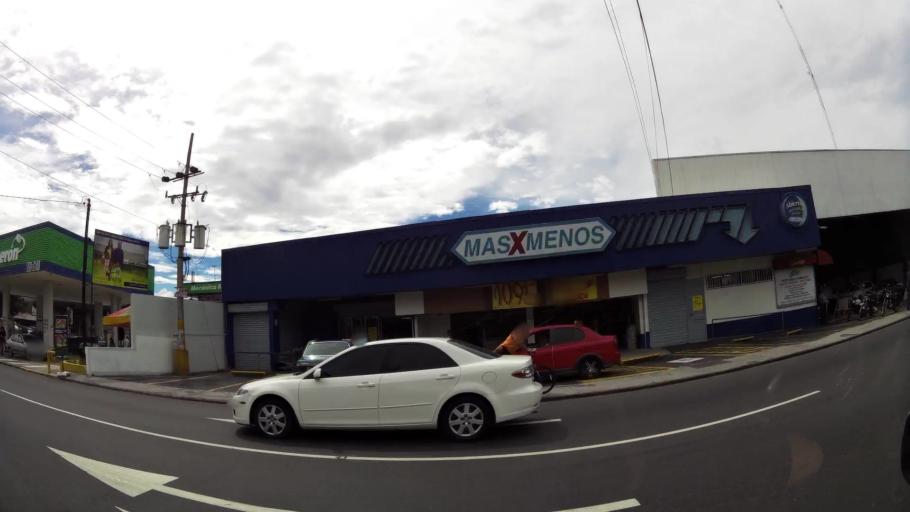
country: CR
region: San Jose
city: San Pedro
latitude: 9.9313
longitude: -84.0470
